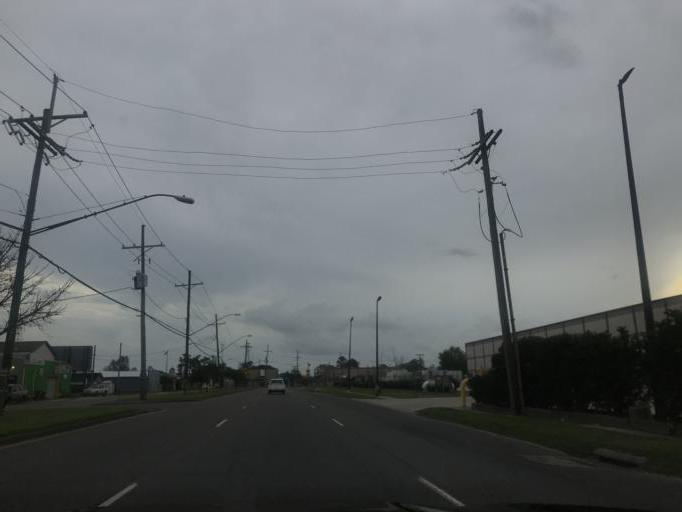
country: US
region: Louisiana
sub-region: Jefferson Parish
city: Jefferson
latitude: 29.9641
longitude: -90.1400
